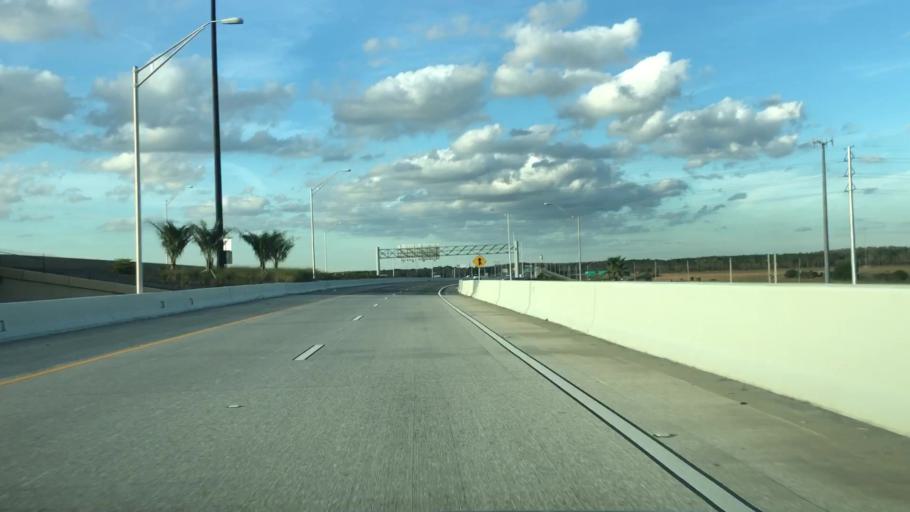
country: US
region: Florida
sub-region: Osceola County
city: Buenaventura Lakes
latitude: 28.3730
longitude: -81.3086
